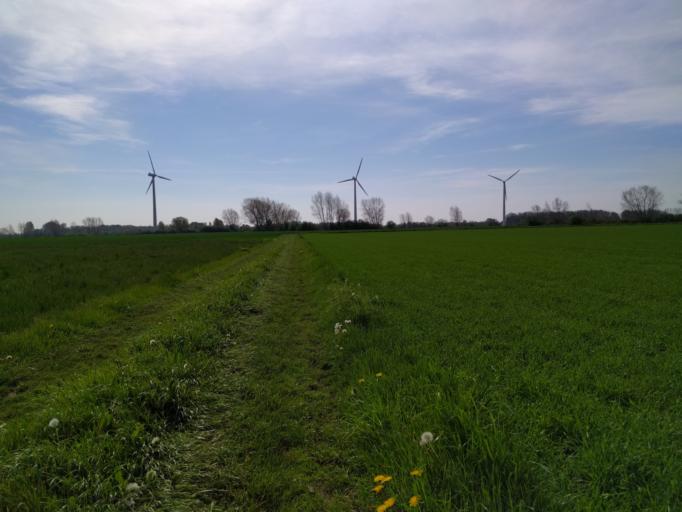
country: DK
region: South Denmark
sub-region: Odense Kommune
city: Bullerup
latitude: 55.4003
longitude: 10.5282
